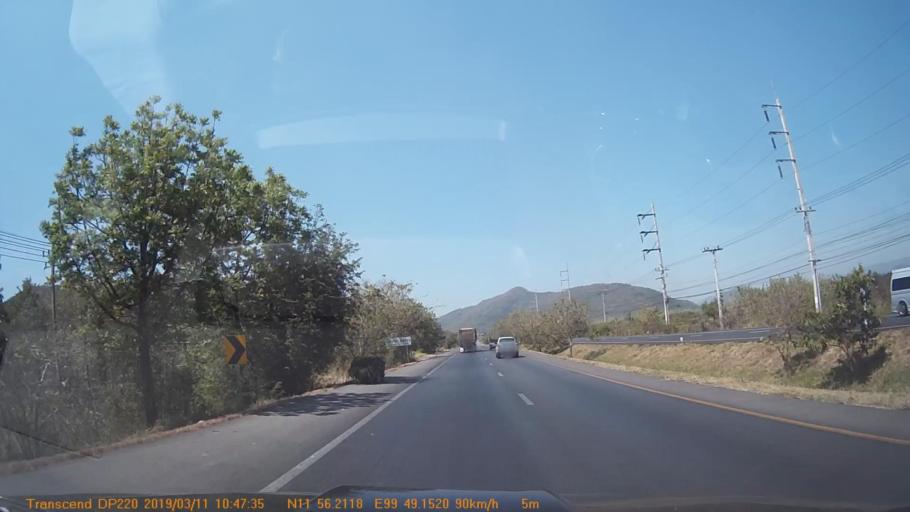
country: TH
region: Prachuap Khiri Khan
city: Prachuap Khiri Khan
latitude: 11.9367
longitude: 99.8189
